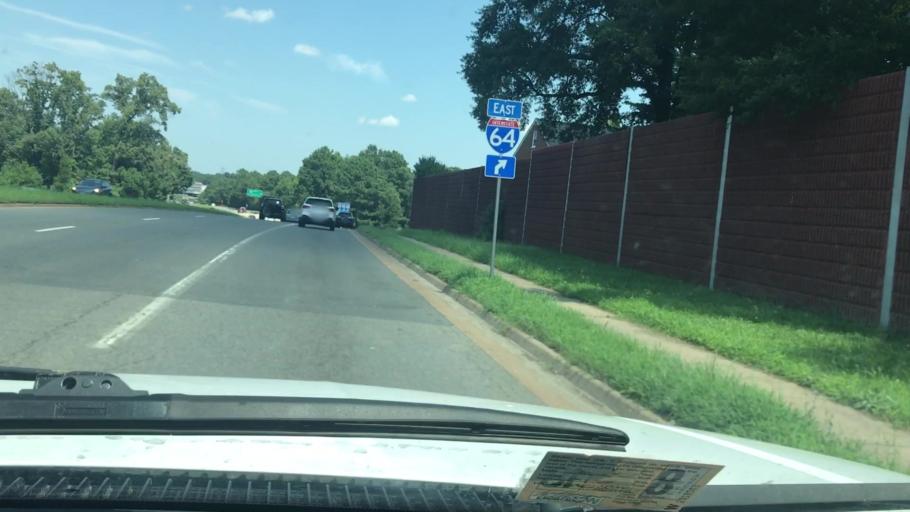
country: US
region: Virginia
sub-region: Henrico County
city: Dumbarton
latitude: 37.5949
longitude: -77.4922
